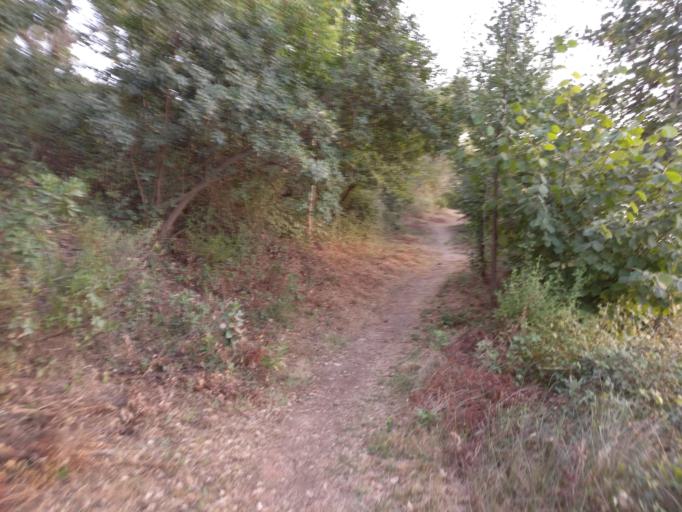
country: PT
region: Beja
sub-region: Odemira
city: Odemira
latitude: 37.7193
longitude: -8.5170
